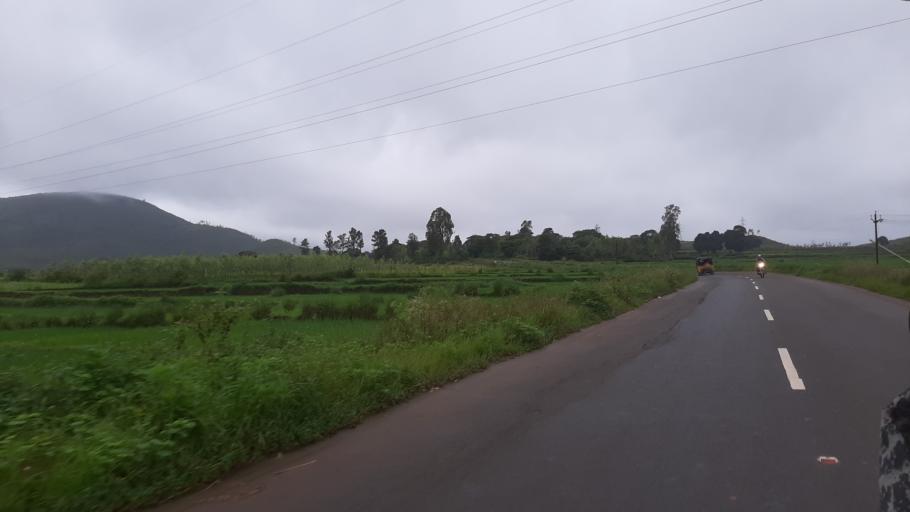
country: IN
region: Andhra Pradesh
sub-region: Vizianagaram District
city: Salur
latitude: 18.3372
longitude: 82.8569
